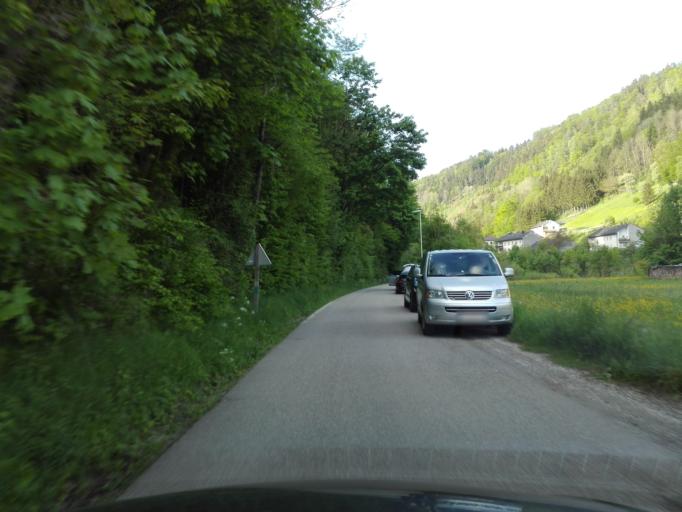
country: AT
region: Upper Austria
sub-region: Politischer Bezirk Rohrbach
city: Atzesberg
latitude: 48.4516
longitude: 13.9193
